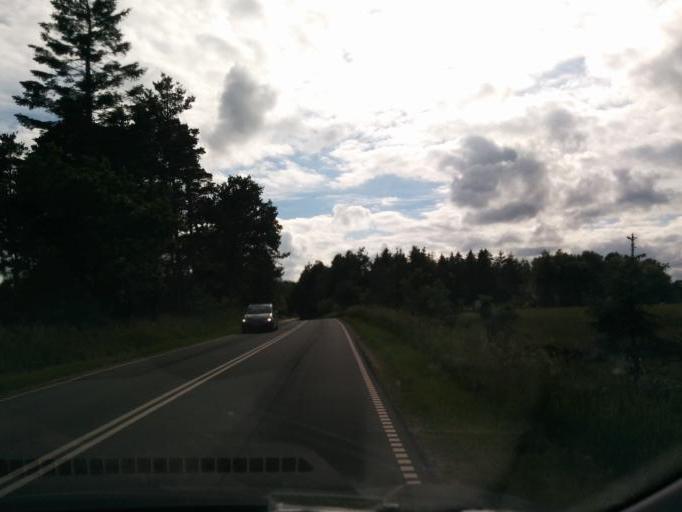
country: DK
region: Central Jutland
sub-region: Syddjurs Kommune
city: Ryomgard
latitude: 56.3533
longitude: 10.4837
